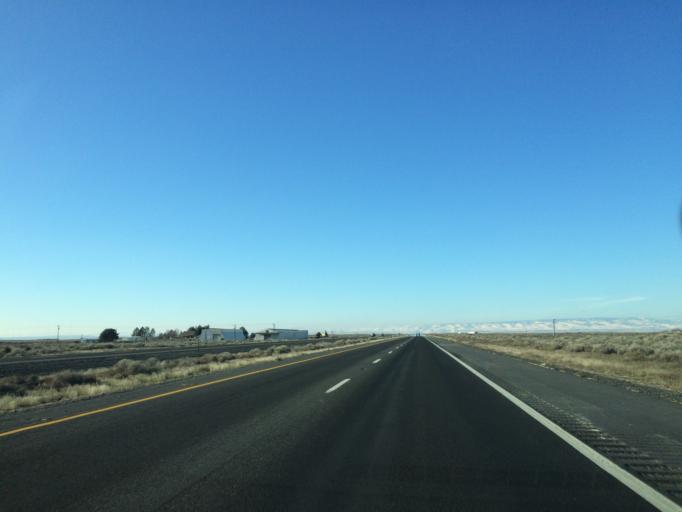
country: US
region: Washington
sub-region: Grant County
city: Royal City
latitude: 47.1039
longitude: -119.6572
